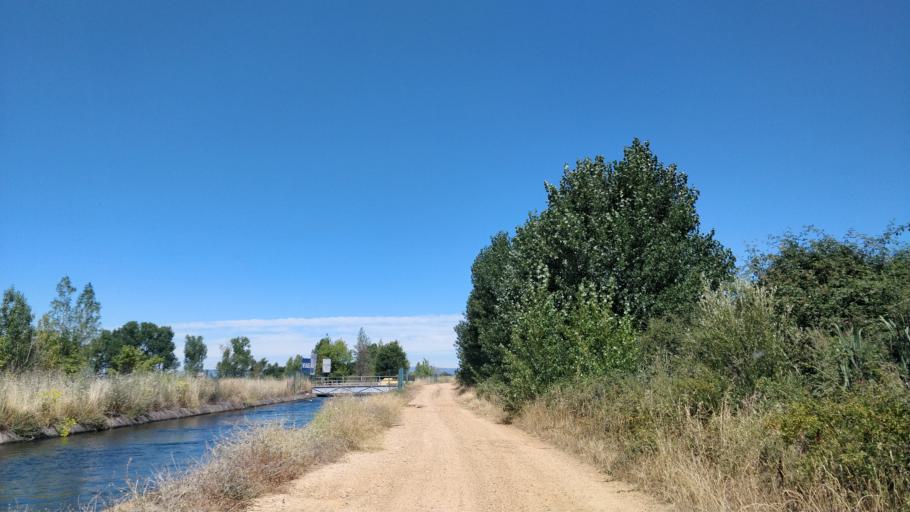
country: ES
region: Castille and Leon
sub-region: Provincia de Leon
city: Bustillo del Paramo
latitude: 42.4798
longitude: -5.8064
